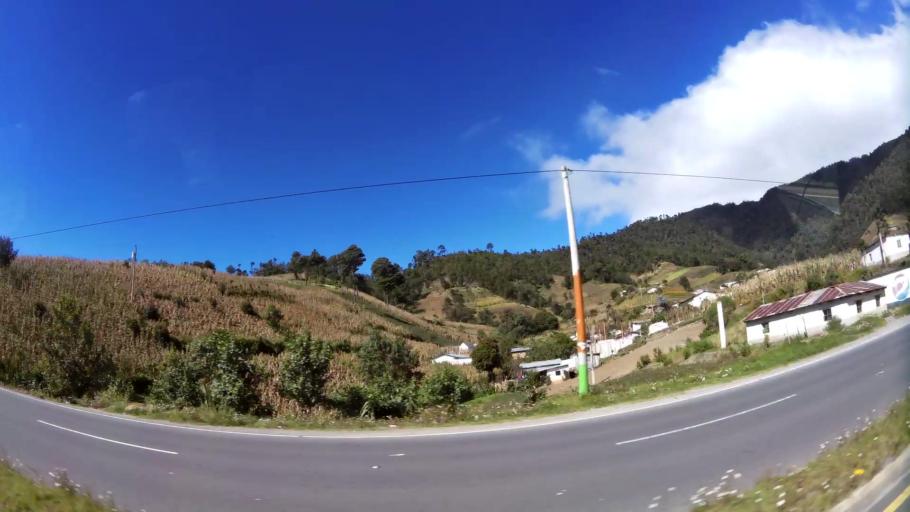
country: GT
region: Solola
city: Concepcion
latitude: 14.8333
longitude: -91.1846
